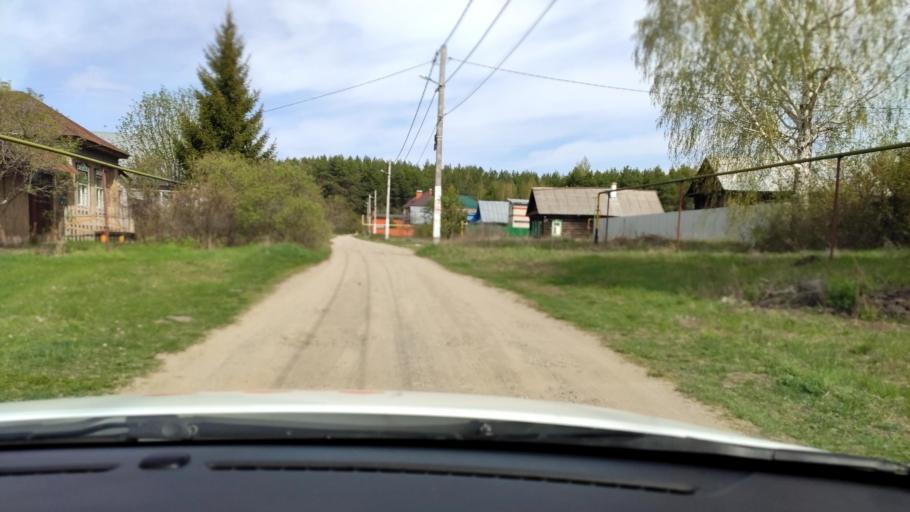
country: RU
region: Tatarstan
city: Osinovo
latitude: 55.8079
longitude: 48.8854
